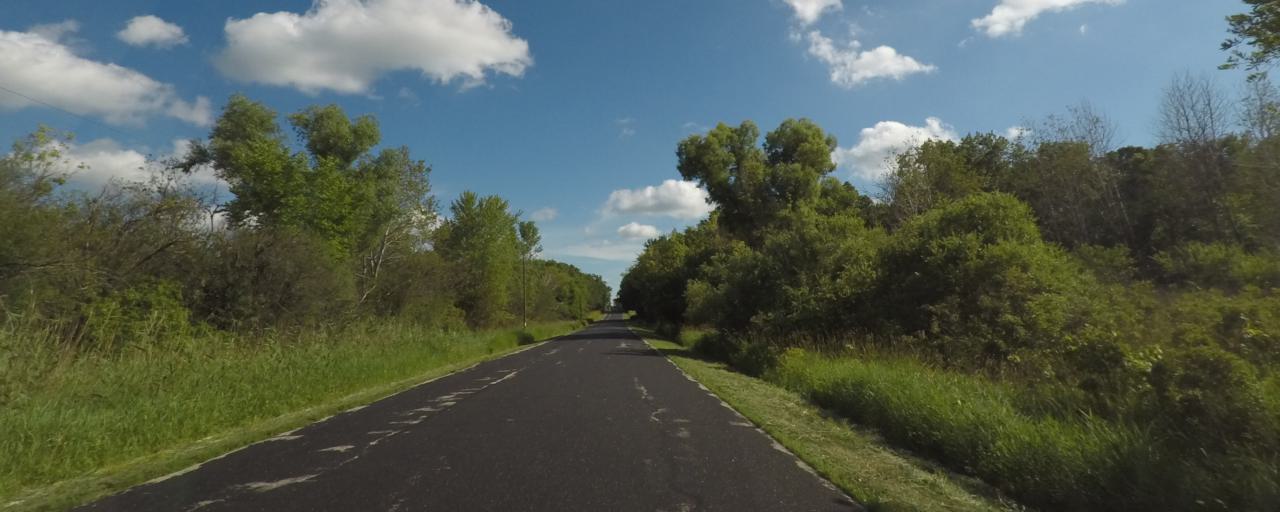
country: US
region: Wisconsin
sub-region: Rock County
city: Edgerton
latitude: 42.8742
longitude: -89.1321
